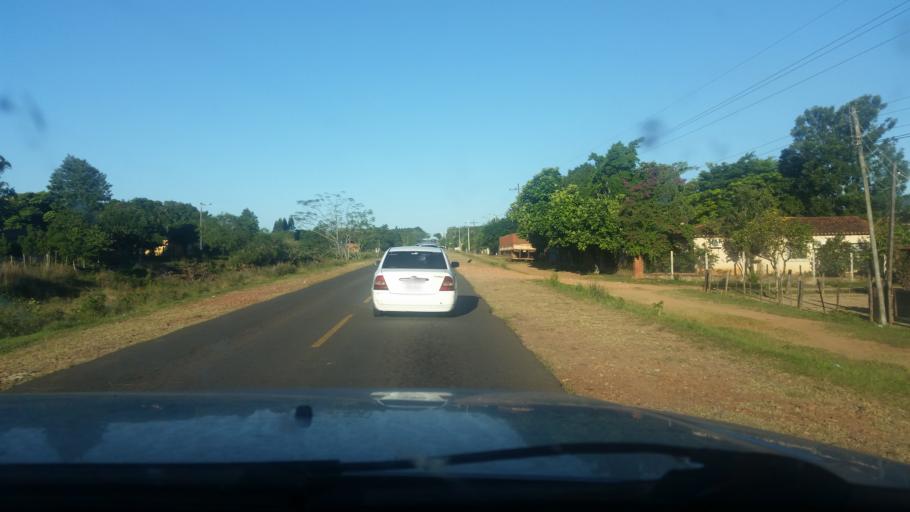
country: PY
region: Guaira
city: Independencia
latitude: -25.7225
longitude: -56.3234
